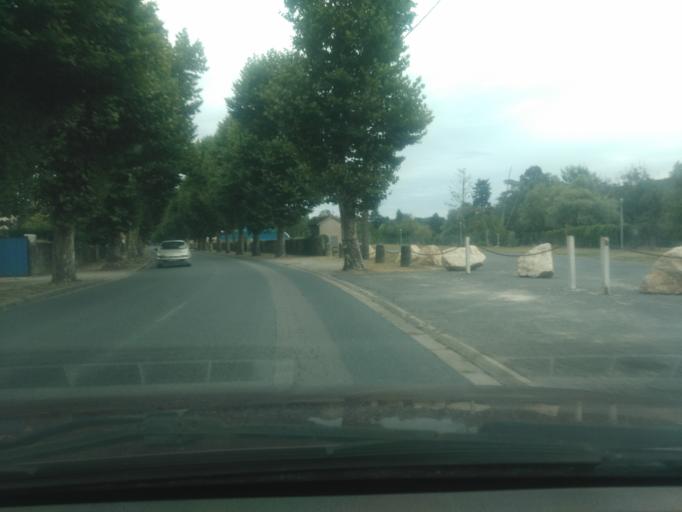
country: FR
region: Centre
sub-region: Departement de l'Indre
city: Le Blanc
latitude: 46.6304
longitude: 1.0654
